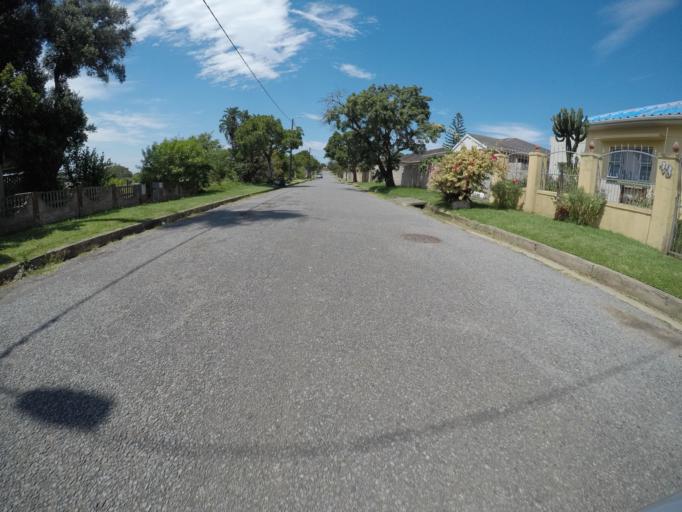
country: ZA
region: Eastern Cape
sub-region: Buffalo City Metropolitan Municipality
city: East London
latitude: -33.0332
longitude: 27.8608
